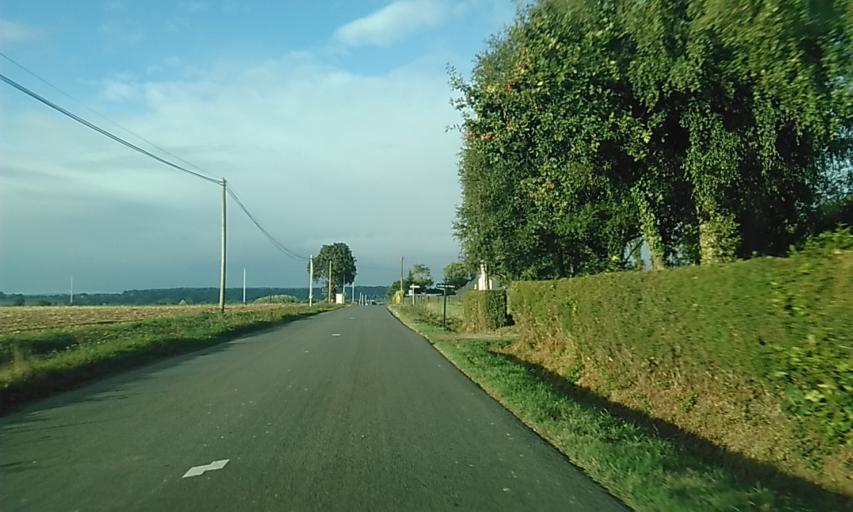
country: FR
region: Brittany
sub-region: Departement d'Ille-et-Vilaine
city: Bedee
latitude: 48.1752
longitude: -1.9841
